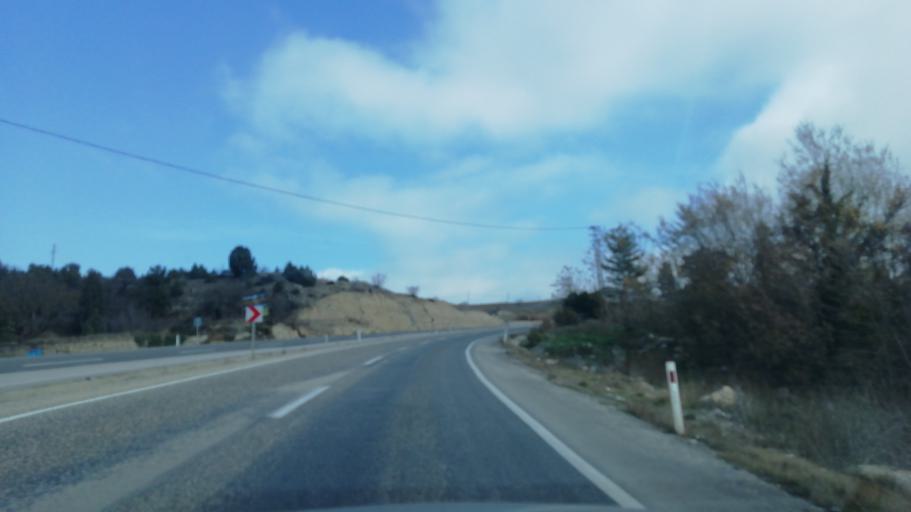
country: TR
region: Karabuk
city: Safranbolu
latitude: 41.2237
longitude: 32.7694
